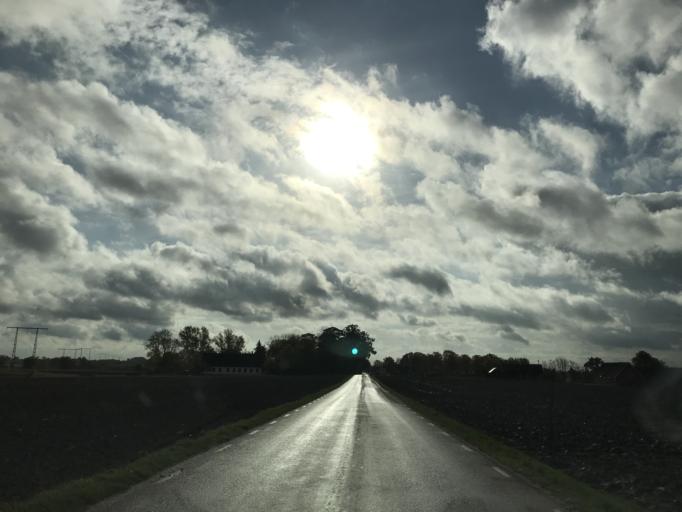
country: SE
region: Skane
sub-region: Svalovs Kommun
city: Teckomatorp
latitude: 55.8745
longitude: 13.1174
